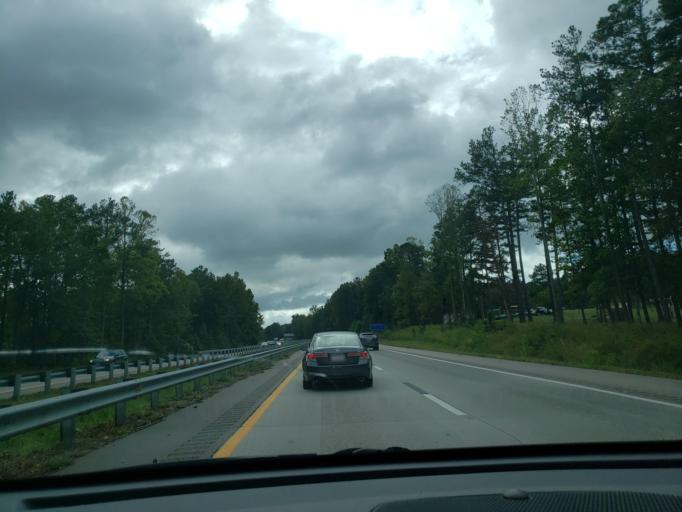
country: US
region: North Carolina
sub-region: Vance County
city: Henderson
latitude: 36.4145
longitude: -78.3191
